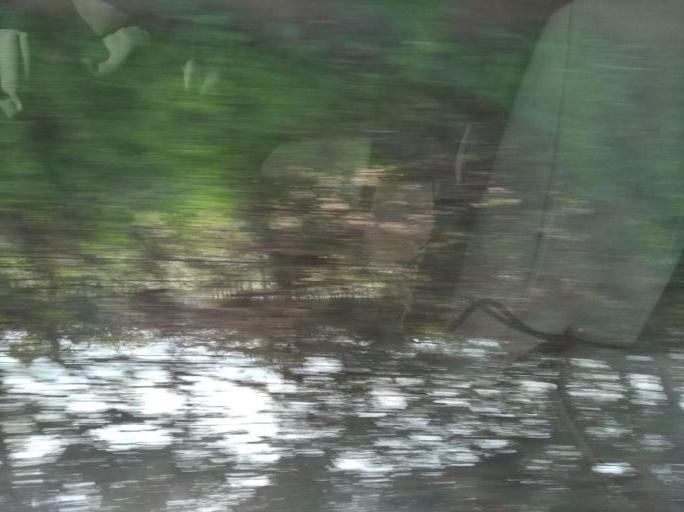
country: CL
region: Valparaiso
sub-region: Provincia de Marga Marga
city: Limache
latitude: -33.0120
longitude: -71.2120
